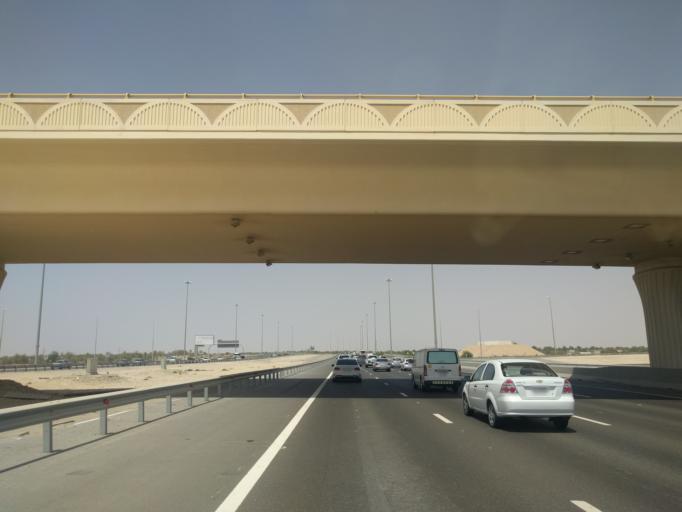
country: AE
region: Abu Dhabi
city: Abu Dhabi
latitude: 24.6960
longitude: 54.7808
